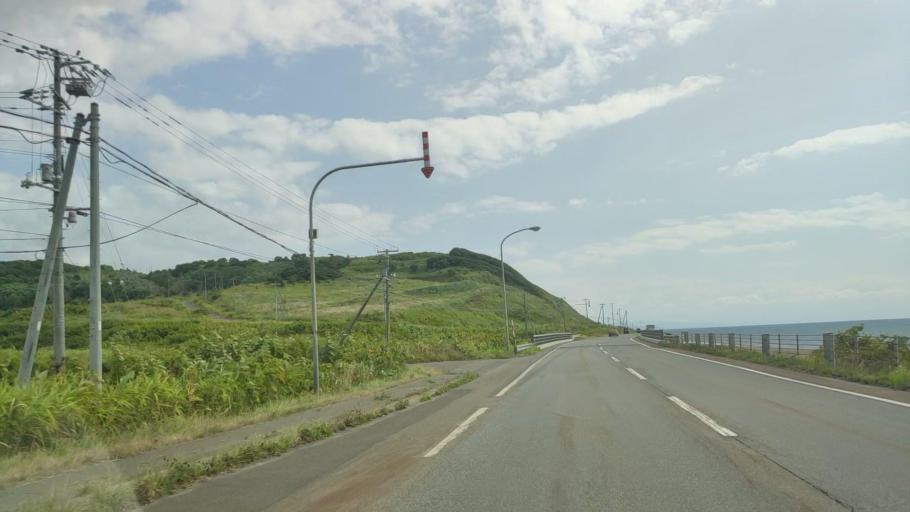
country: JP
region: Hokkaido
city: Rumoi
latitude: 44.1018
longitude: 141.6606
